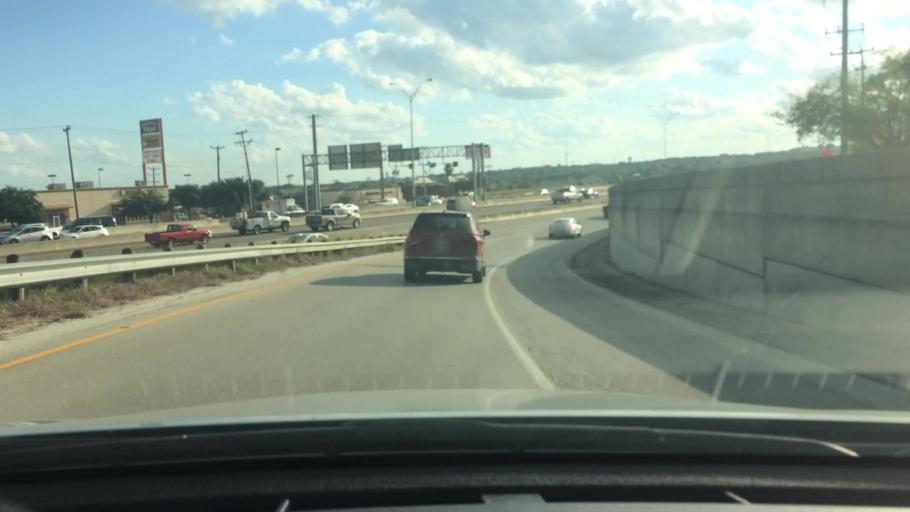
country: US
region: Texas
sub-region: Bexar County
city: Live Oak
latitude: 29.5670
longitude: -98.3351
